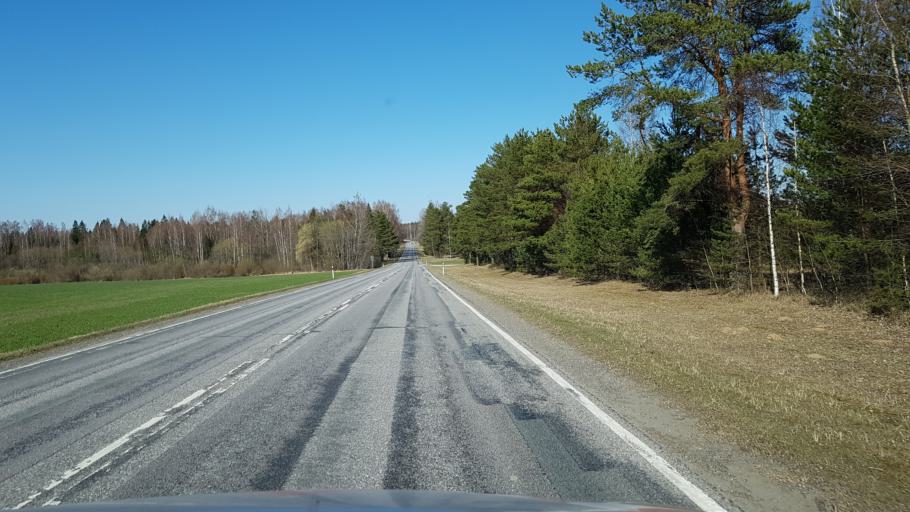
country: EE
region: Jogevamaa
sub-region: Tabivere vald
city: Tabivere
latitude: 58.5880
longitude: 26.7639
